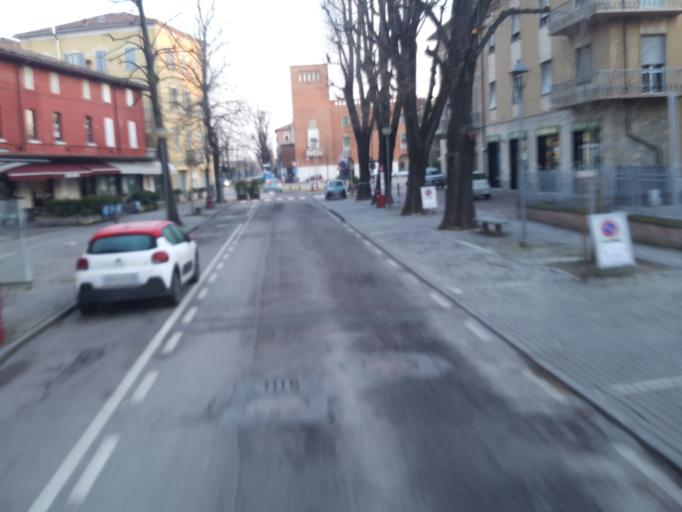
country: IT
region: Emilia-Romagna
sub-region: Provincia di Parma
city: Sorbolo
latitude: 44.8453
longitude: 10.4481
